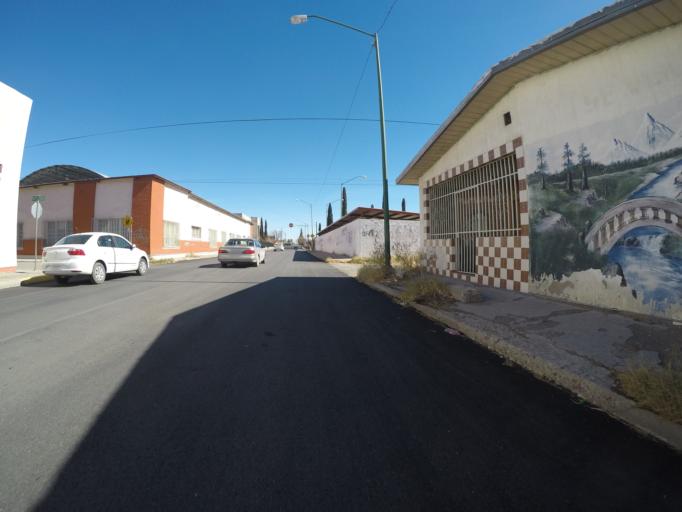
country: MX
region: Chihuahua
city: Ciudad Juarez
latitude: 31.7408
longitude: -106.4705
